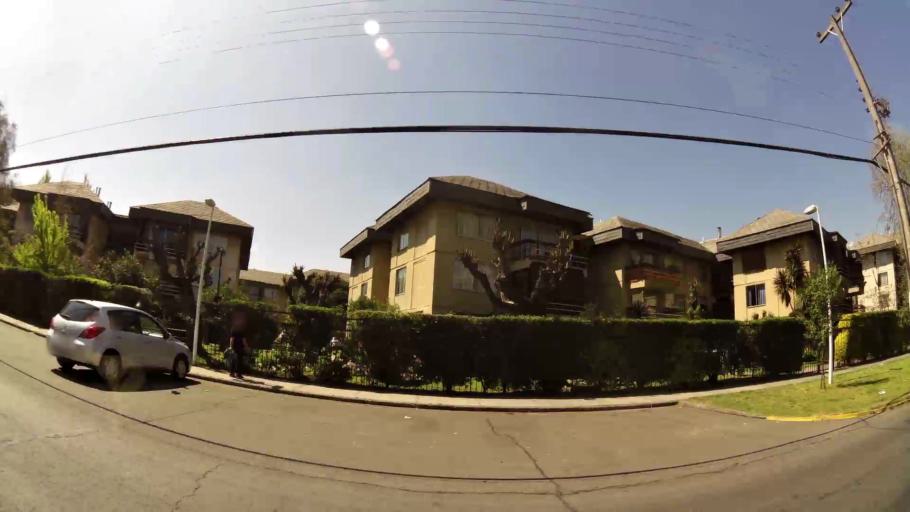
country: CL
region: Santiago Metropolitan
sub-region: Provincia de Santiago
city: Villa Presidente Frei, Nunoa, Santiago, Chile
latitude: -33.4235
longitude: -70.5533
